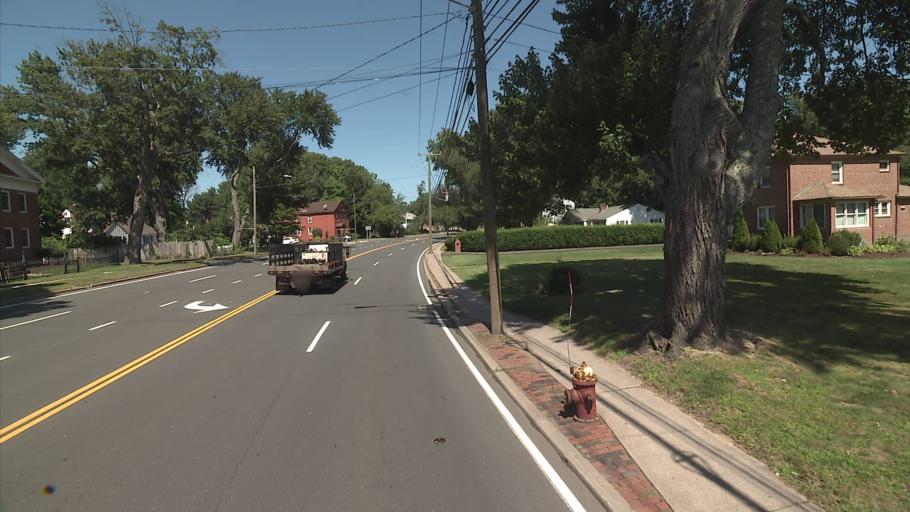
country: US
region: Connecticut
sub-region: Hartford County
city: Windsor
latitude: 41.8297
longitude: -72.6558
